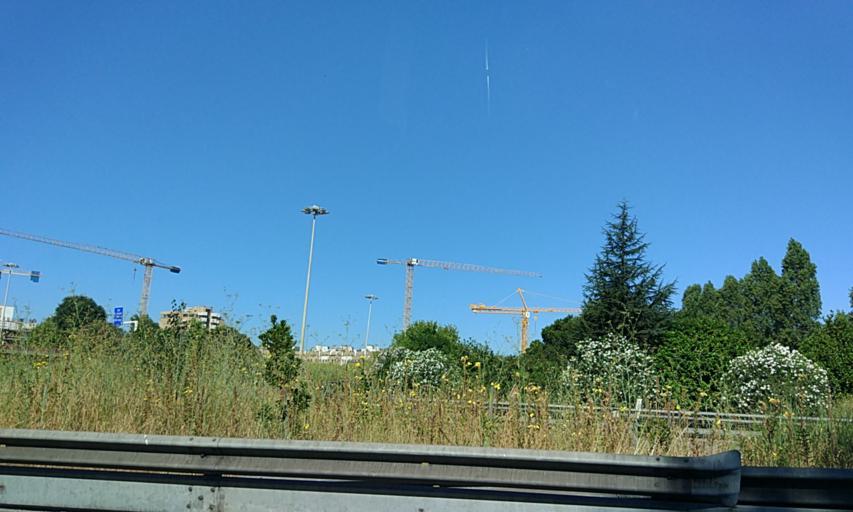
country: PT
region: Porto
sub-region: Matosinhos
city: Senhora da Hora
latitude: 41.1688
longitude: -8.6364
